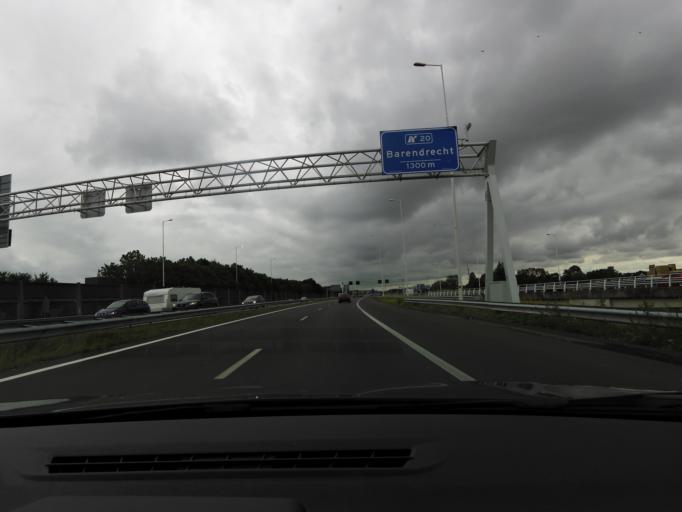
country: NL
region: South Holland
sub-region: Gemeente Barendrecht
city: Barendrecht
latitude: 51.8615
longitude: 4.5159
